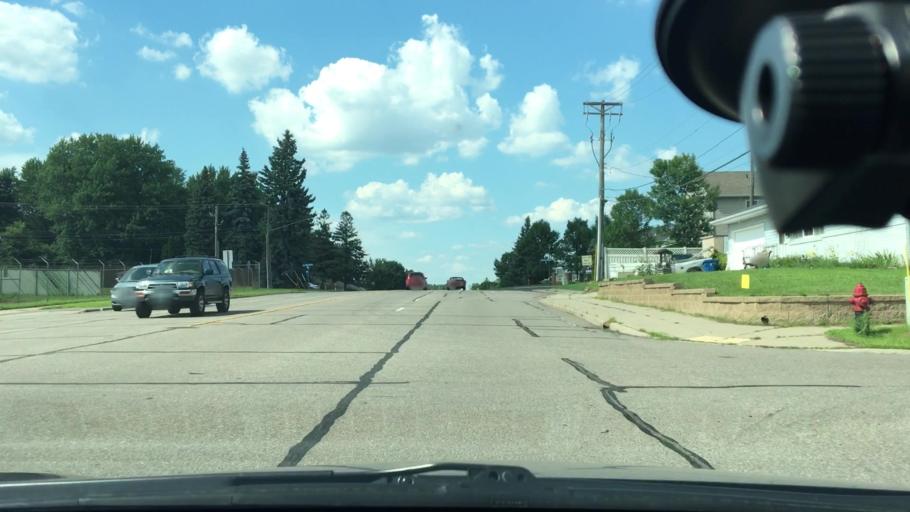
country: US
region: Minnesota
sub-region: Hennepin County
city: New Hope
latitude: 45.0502
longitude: -93.3803
